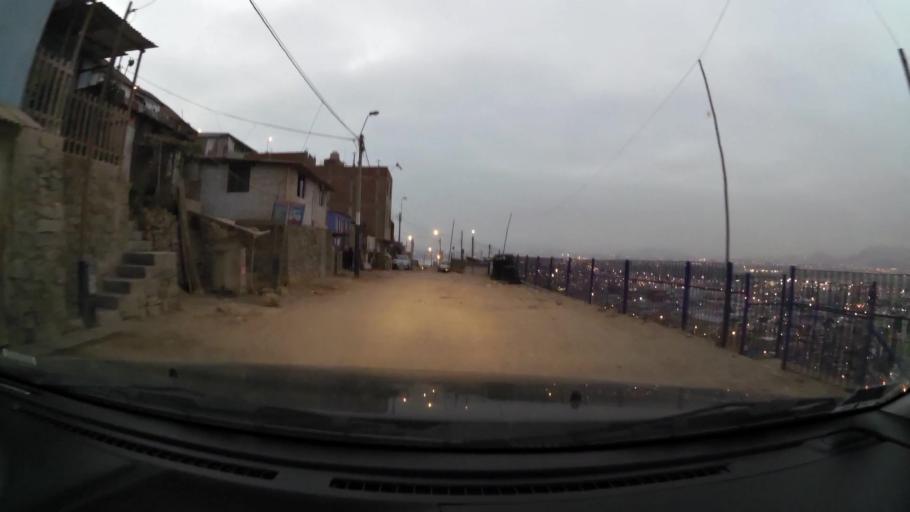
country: PE
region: Lima
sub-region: Lima
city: Surco
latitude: -12.1844
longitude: -77.0214
